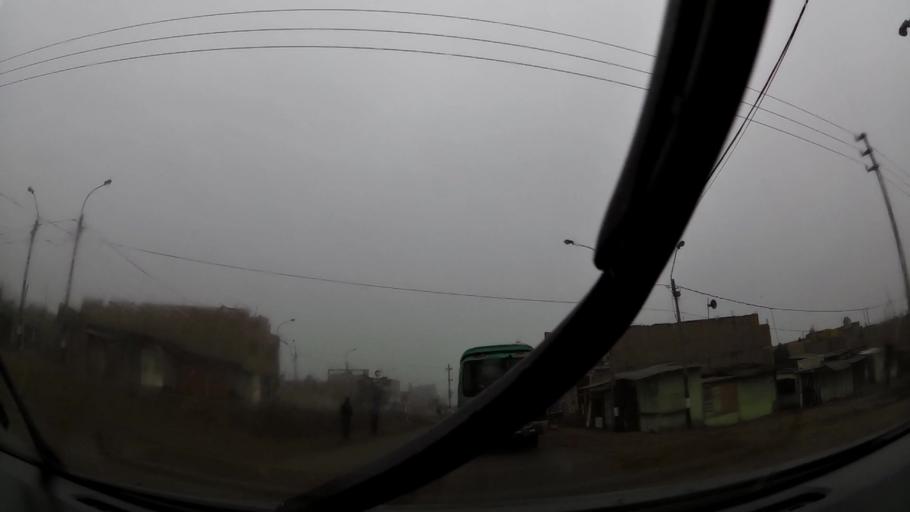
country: PE
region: Lima
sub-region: Lima
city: Santa Rosa
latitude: -11.8309
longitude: -77.1377
